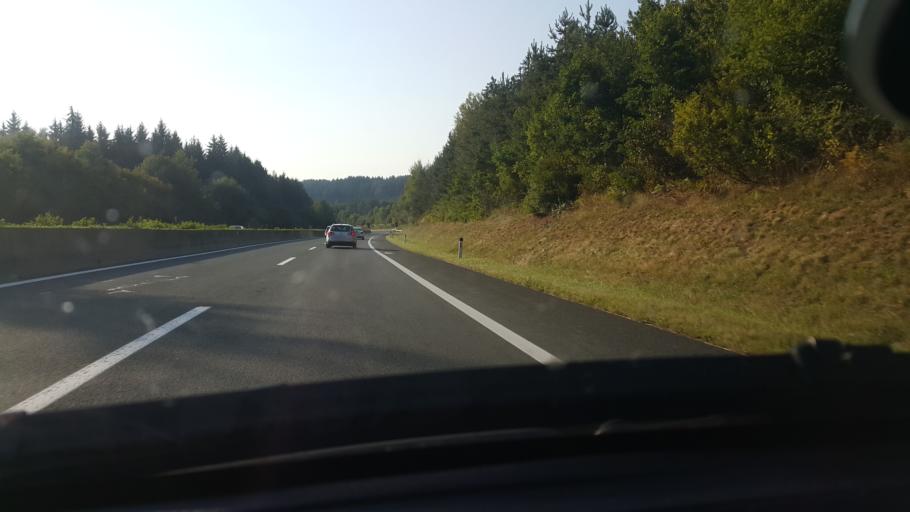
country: AT
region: Carinthia
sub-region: Politischer Bezirk Klagenfurt Land
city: Grafenstein
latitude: 46.6498
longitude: 14.5411
